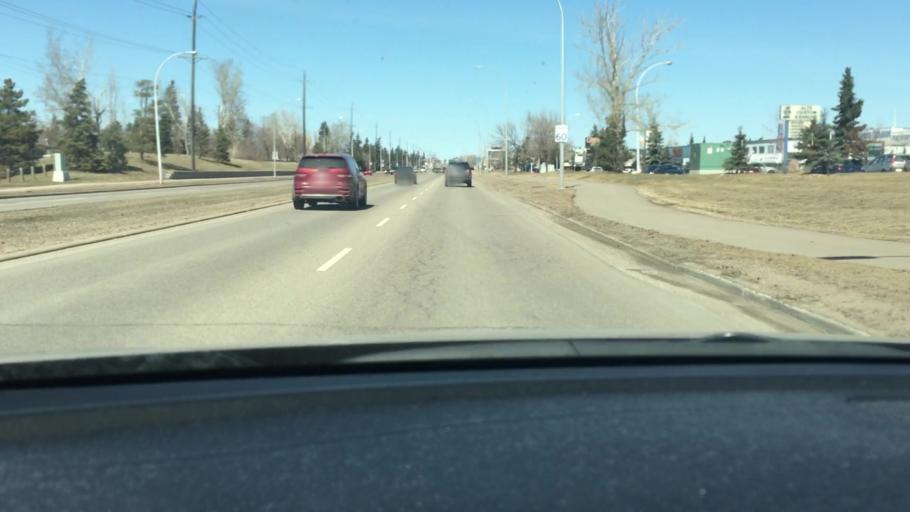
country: CA
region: Alberta
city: Edmonton
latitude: 53.5277
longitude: -113.4184
